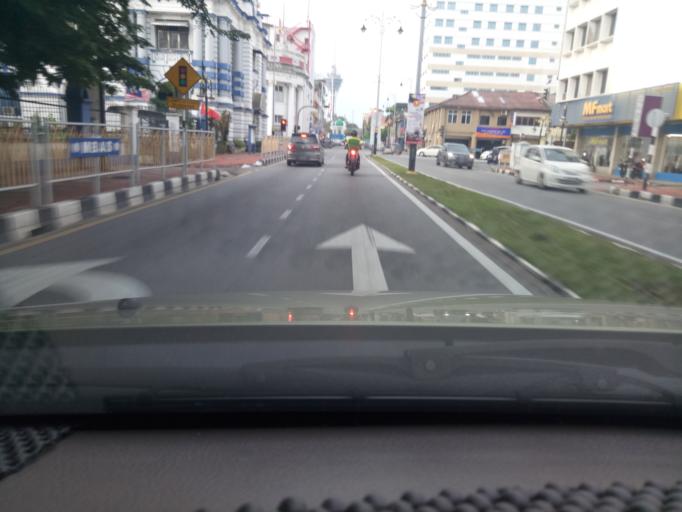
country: MY
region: Kedah
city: Alor Setar
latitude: 6.1163
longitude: 100.3653
